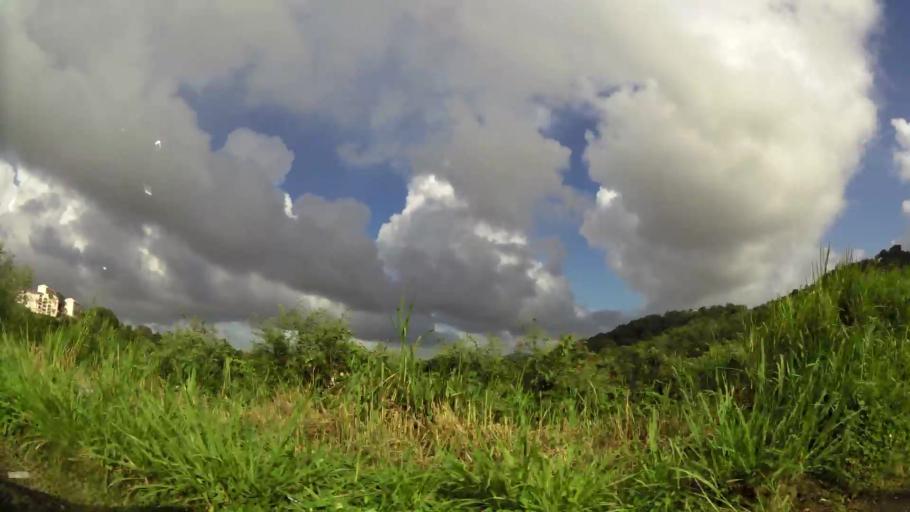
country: MQ
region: Martinique
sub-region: Martinique
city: Ducos
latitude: 14.5691
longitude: -60.9635
